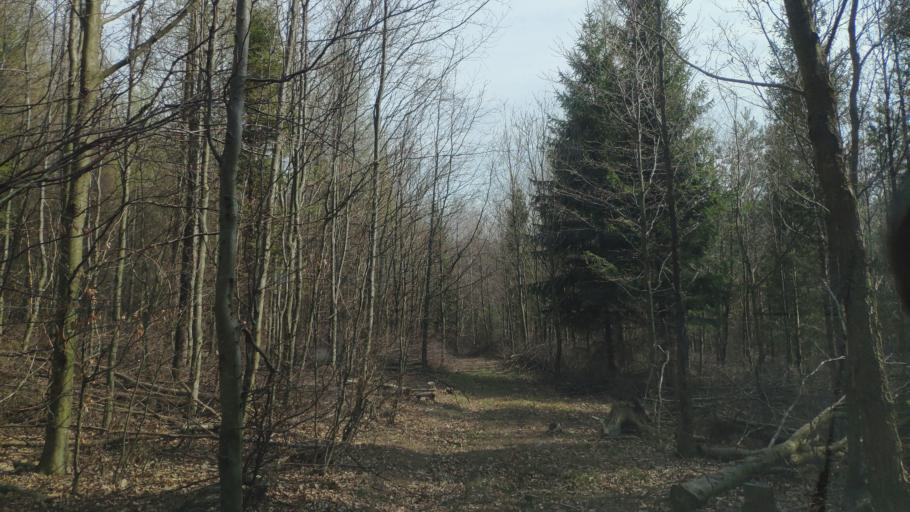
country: SK
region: Kosicky
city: Moldava nad Bodvou
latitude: 48.7444
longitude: 21.0333
